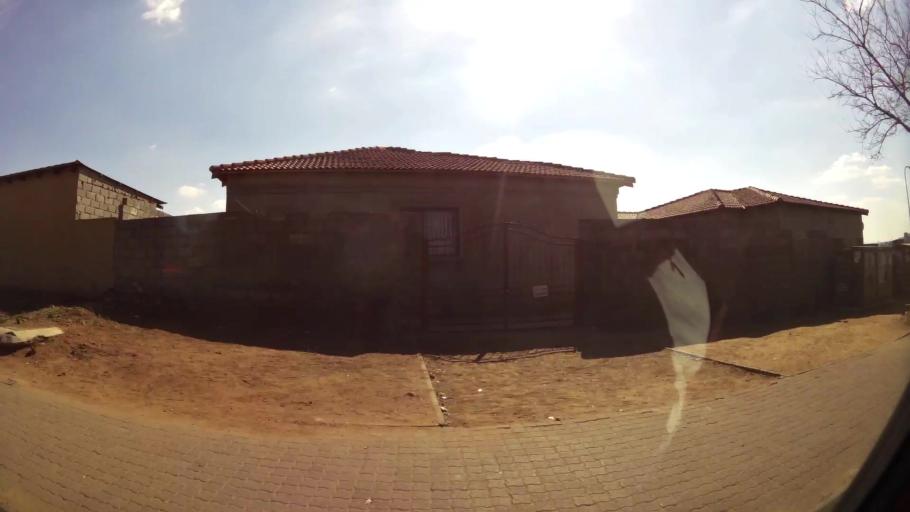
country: ZA
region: Gauteng
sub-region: City of Johannesburg Metropolitan Municipality
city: Soweto
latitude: -26.2349
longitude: 27.9120
